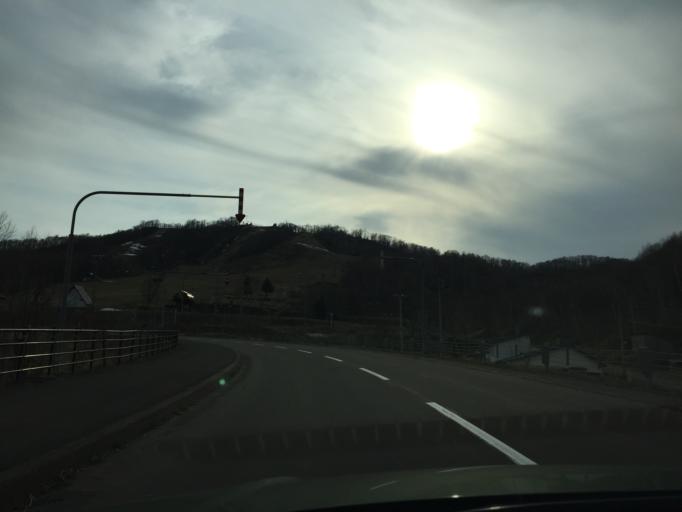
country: JP
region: Hokkaido
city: Utashinai
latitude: 43.5228
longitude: 142.0211
